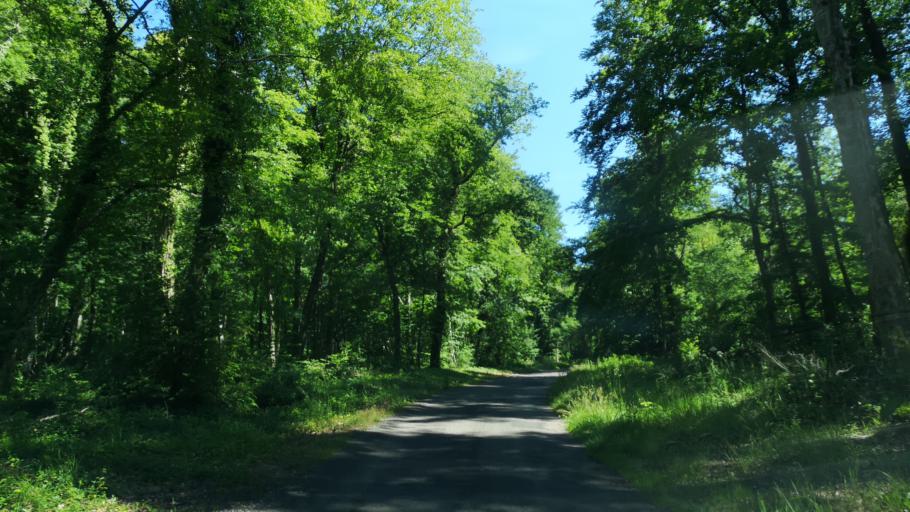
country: FR
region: Lorraine
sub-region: Departement de la Meuse
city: Vigneulles-les-Hattonchatel
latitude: 49.0259
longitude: 5.6454
